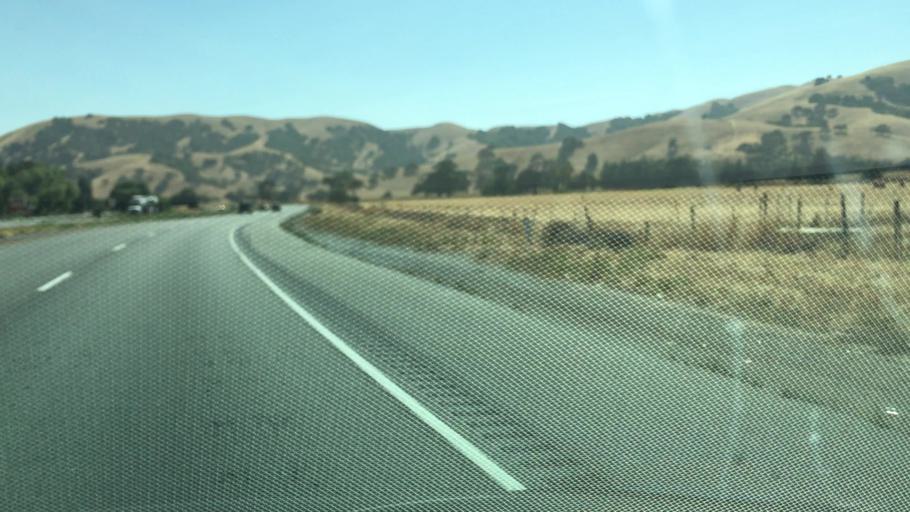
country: US
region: California
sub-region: San Benito County
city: Hollister
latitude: 36.9991
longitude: -121.3749
